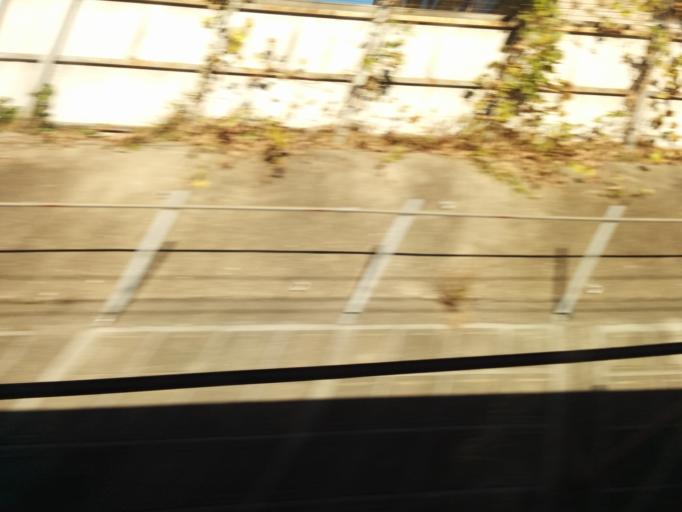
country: JP
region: Kanagawa
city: Minami-rinkan
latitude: 35.4672
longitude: 139.5463
